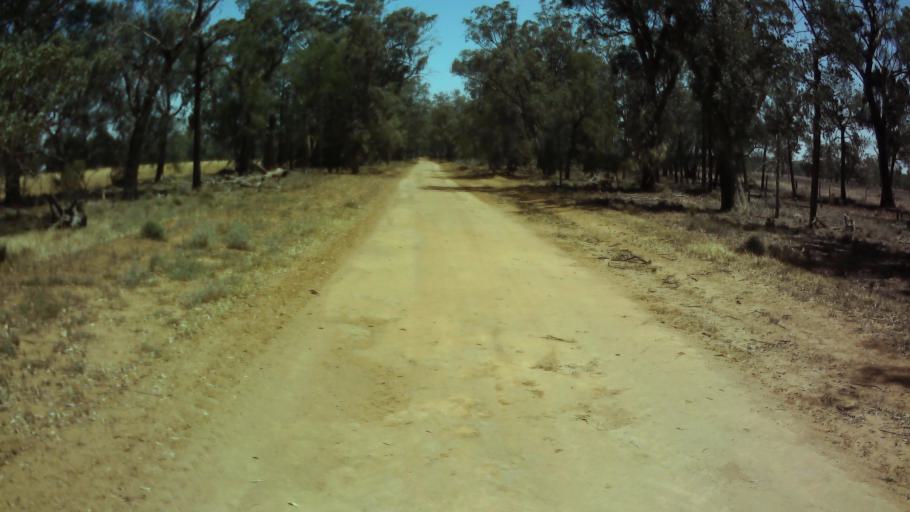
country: AU
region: New South Wales
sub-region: Weddin
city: Grenfell
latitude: -34.0426
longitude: 147.8437
